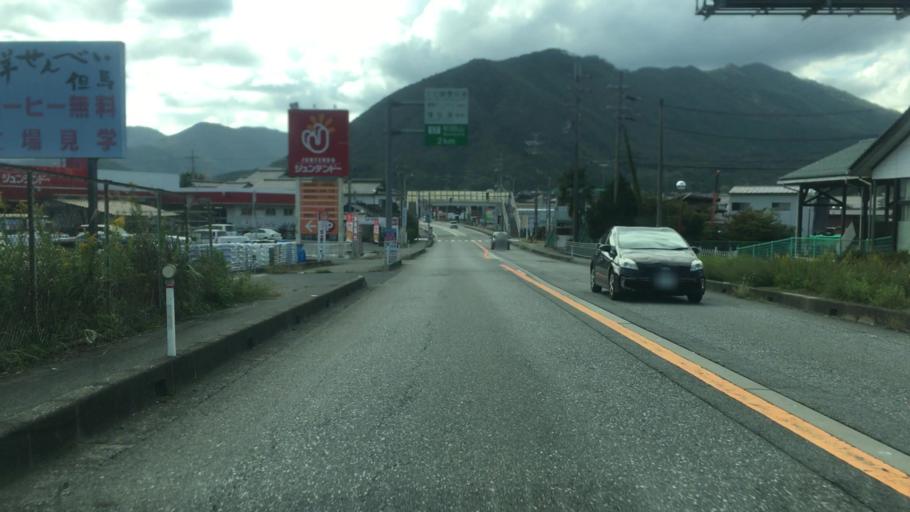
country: JP
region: Hyogo
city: Toyooka
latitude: 35.3300
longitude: 134.8584
